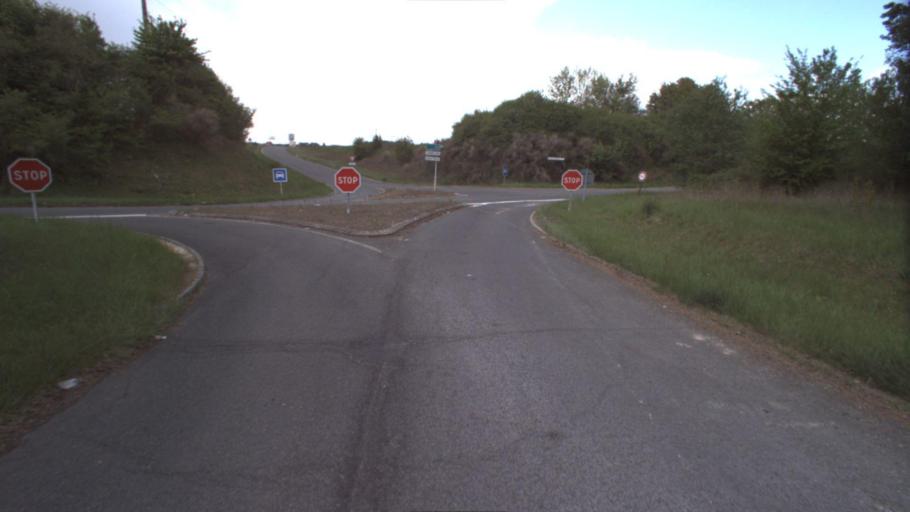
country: FR
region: Ile-de-France
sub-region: Departement de Seine-et-Marne
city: Rozay-en-Brie
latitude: 48.6850
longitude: 2.9377
